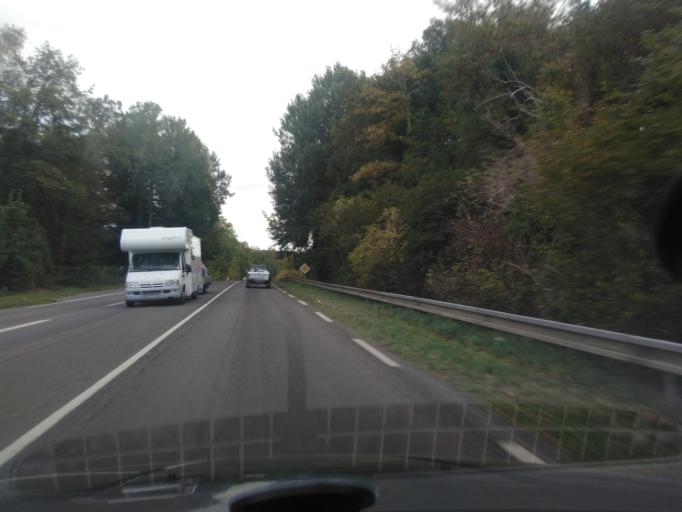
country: FR
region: Picardie
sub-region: Departement de l'Aisne
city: Laon
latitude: 49.5638
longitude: 3.5916
